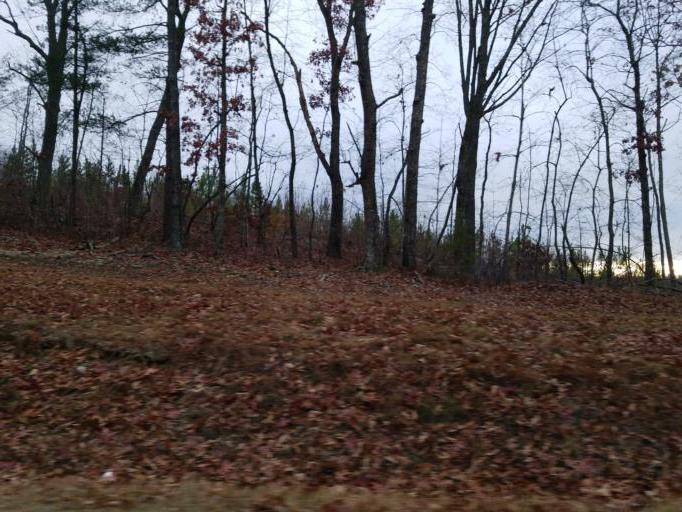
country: US
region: Georgia
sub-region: Dawson County
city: Dawsonville
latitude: 34.4318
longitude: -84.0752
